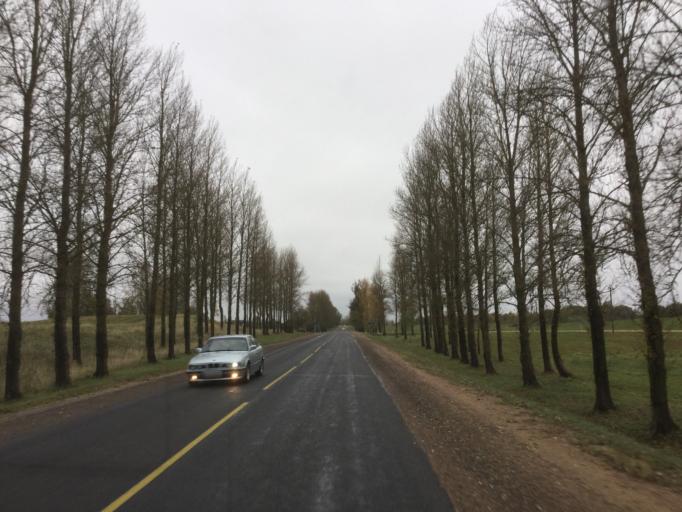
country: BY
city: Novolukoml'
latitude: 54.7179
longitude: 29.1406
